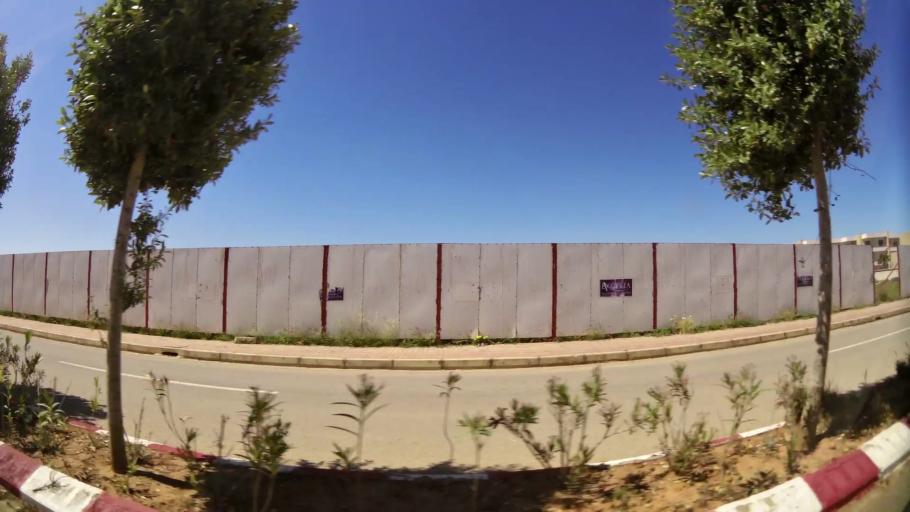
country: MA
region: Oriental
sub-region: Berkane-Taourirt
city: Madagh
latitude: 35.1090
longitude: -2.3130
